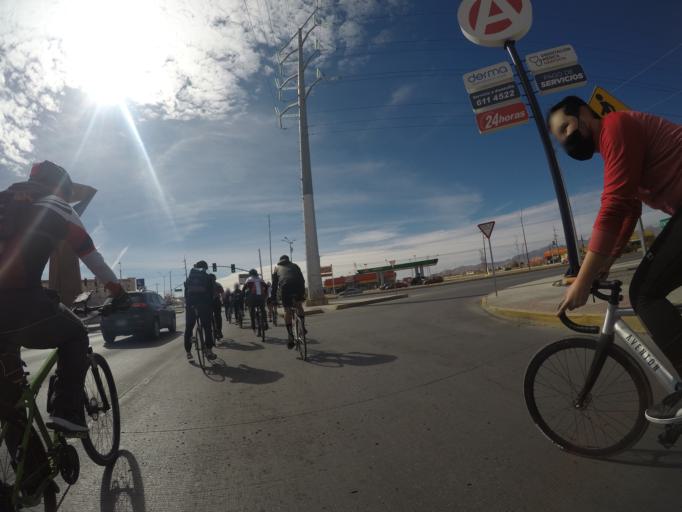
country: MX
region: Chihuahua
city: Ciudad Juarez
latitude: 31.6935
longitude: -106.4040
